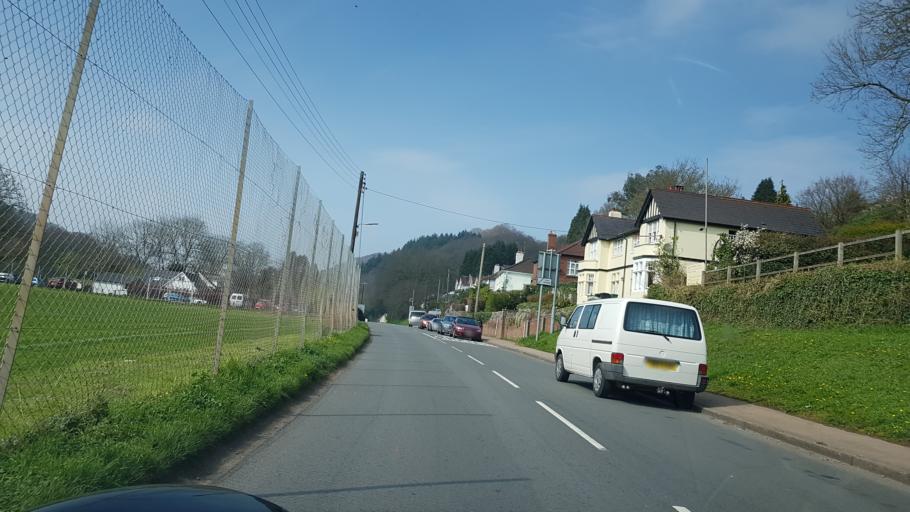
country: GB
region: Wales
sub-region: Monmouthshire
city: Monmouth
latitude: 51.7857
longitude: -2.6725
